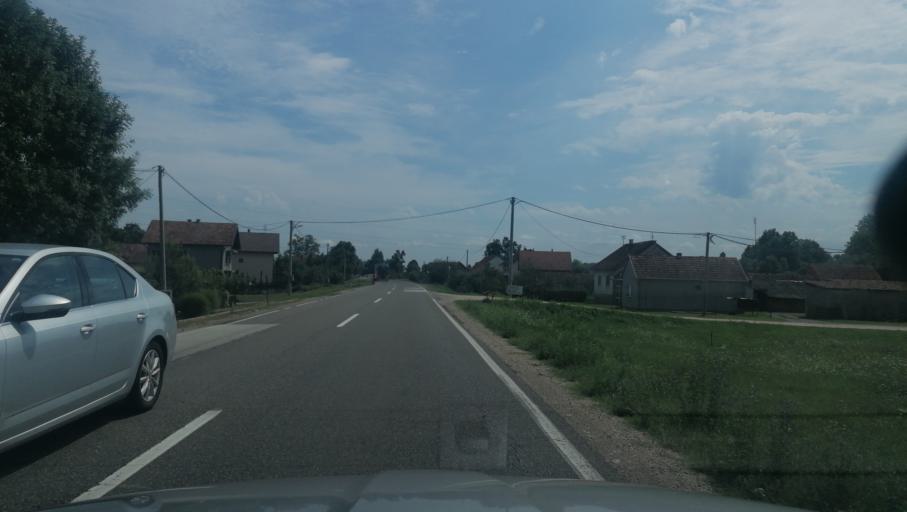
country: BA
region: Republika Srpska
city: Bosanski Samac
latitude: 45.0437
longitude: 18.4884
